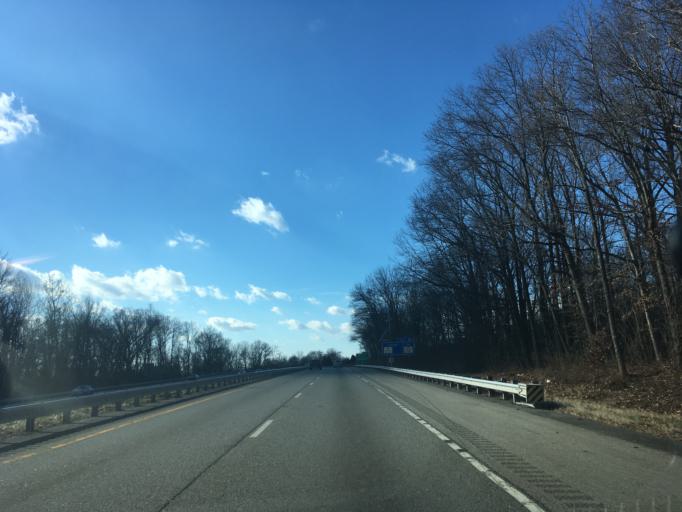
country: US
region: Delaware
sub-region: New Castle County
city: Bellefonte
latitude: 39.7764
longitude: -75.5187
